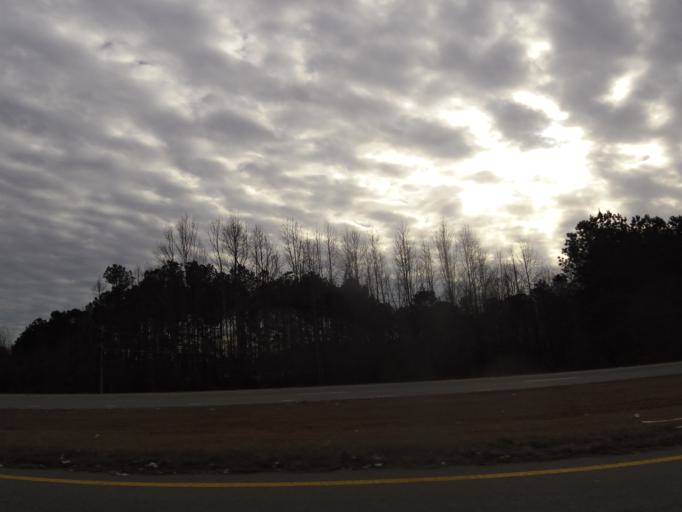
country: US
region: North Carolina
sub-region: Hertford County
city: Murfreesboro
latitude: 36.4278
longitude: -77.1205
